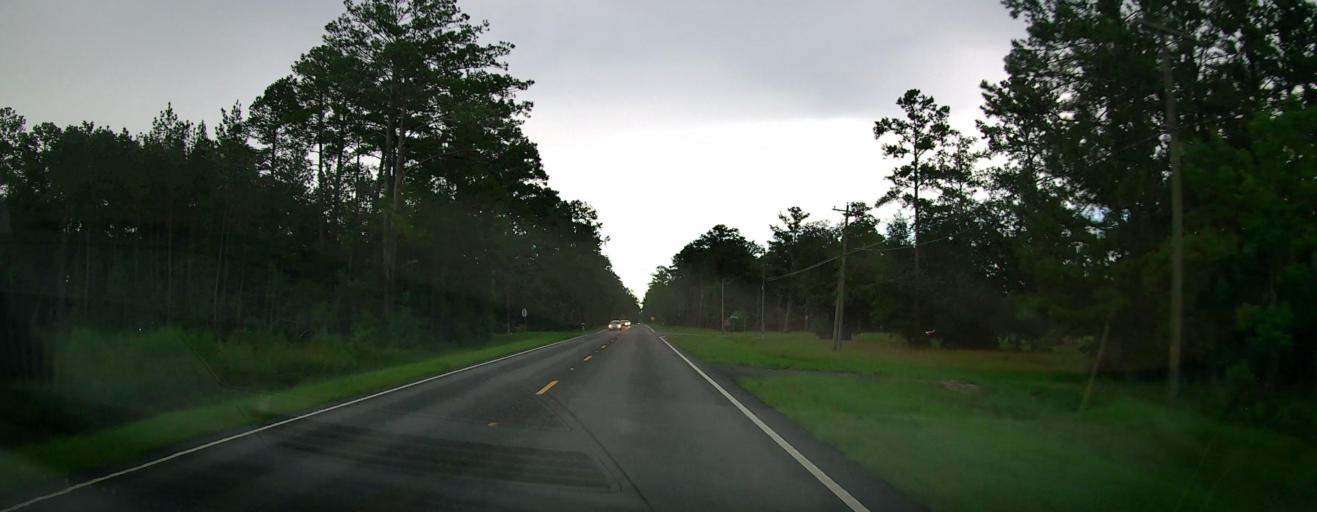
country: US
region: Georgia
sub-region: Glynn County
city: Dock Junction
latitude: 31.2896
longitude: -81.6859
